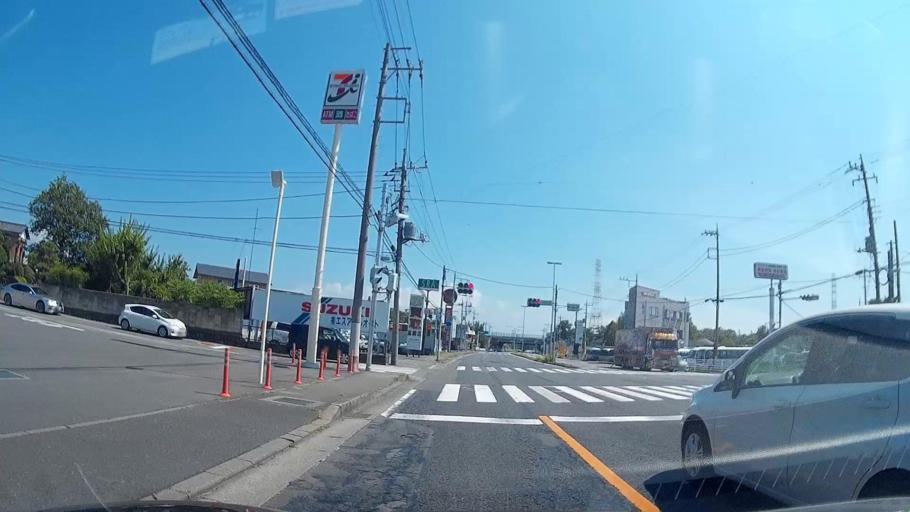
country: JP
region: Gunma
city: Takasaki
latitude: 36.3716
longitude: 139.0253
